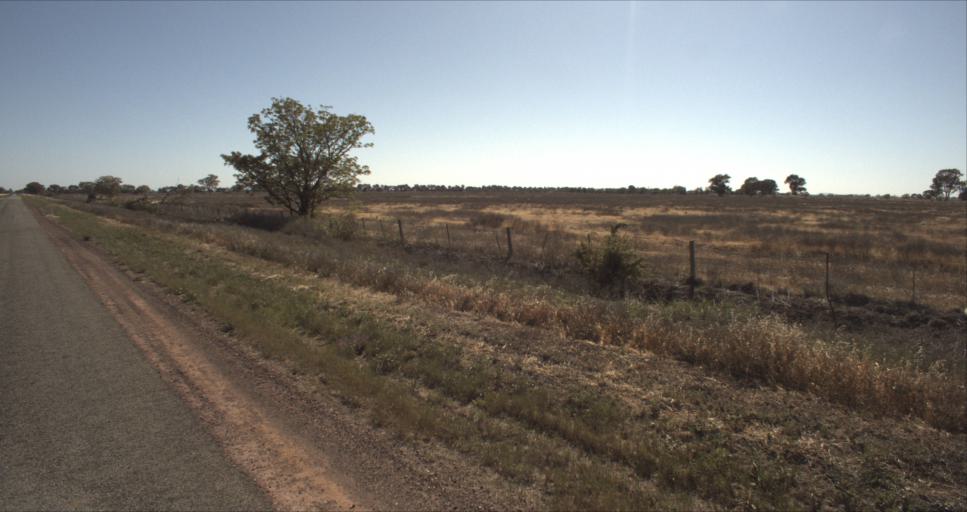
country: AU
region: New South Wales
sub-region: Leeton
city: Leeton
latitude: -34.5869
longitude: 146.2605
